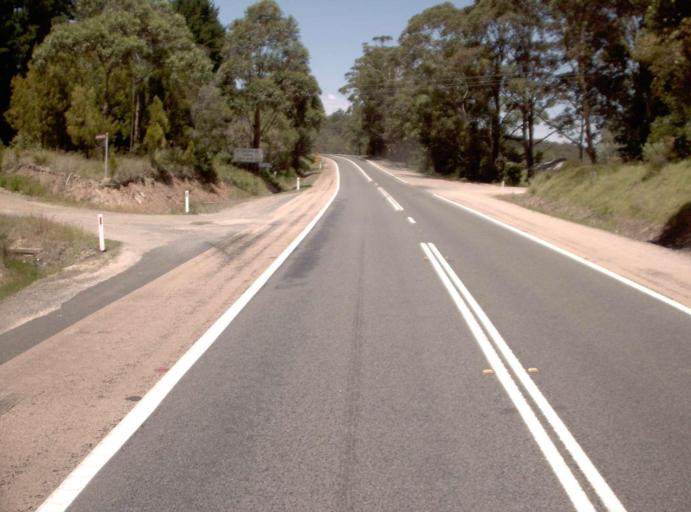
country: AU
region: Victoria
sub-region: East Gippsland
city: Lakes Entrance
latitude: -37.7047
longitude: 148.5670
